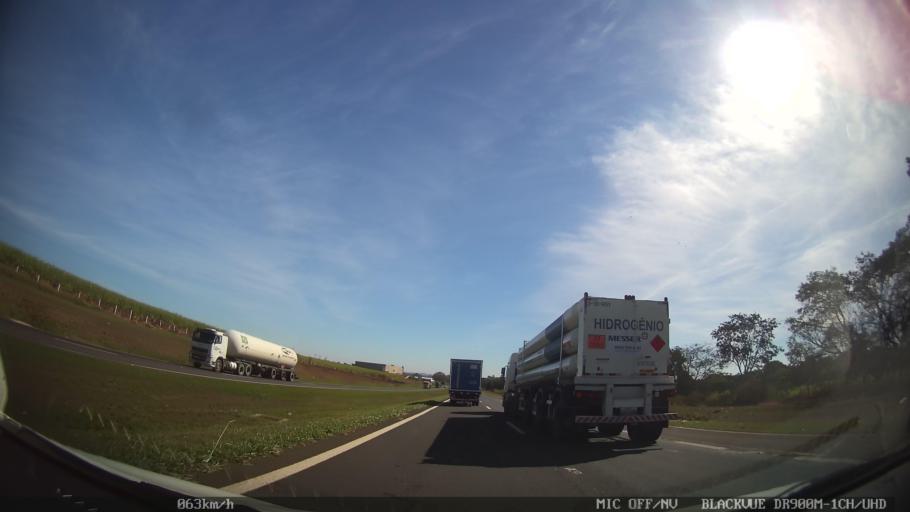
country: BR
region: Sao Paulo
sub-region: Leme
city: Leme
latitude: -22.1439
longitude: -47.4014
